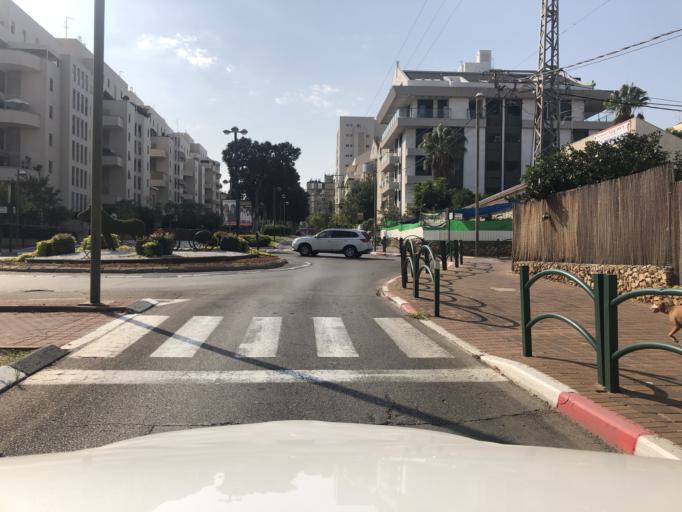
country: IL
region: Central District
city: Kfar Saba
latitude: 32.1786
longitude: 34.9032
